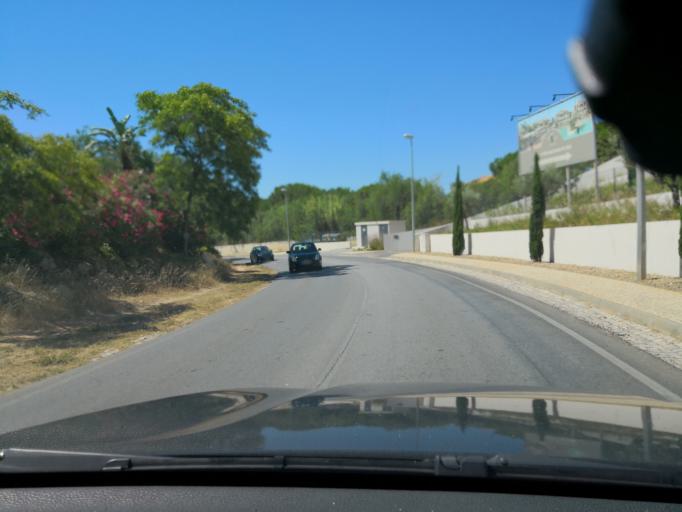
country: PT
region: Faro
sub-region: Loule
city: Vilamoura
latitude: 37.0928
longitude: -8.1027
